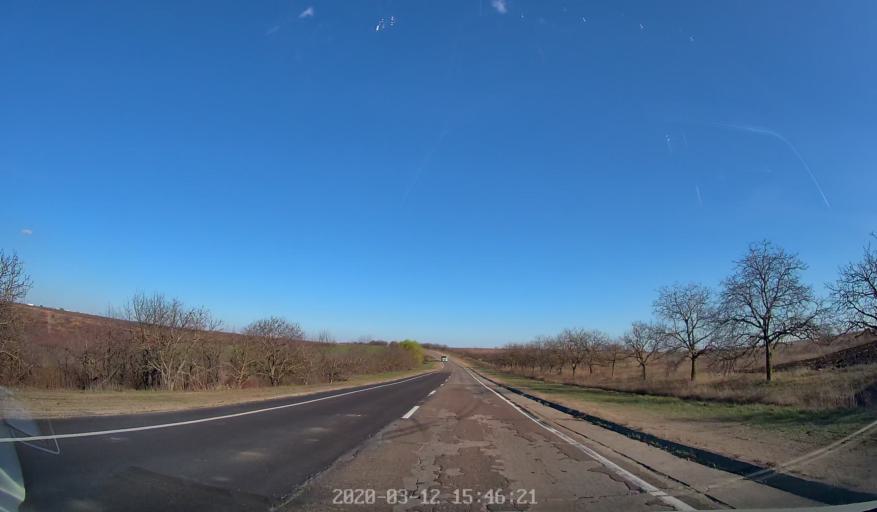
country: MD
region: Chisinau
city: Stauceni
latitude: 47.1000
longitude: 28.8912
